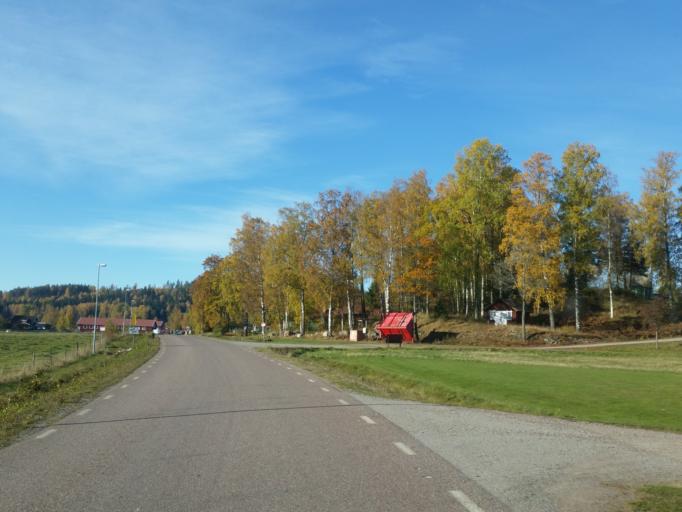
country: SE
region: Dalarna
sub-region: Borlange Kommun
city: Ornas
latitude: 60.4469
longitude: 15.6332
